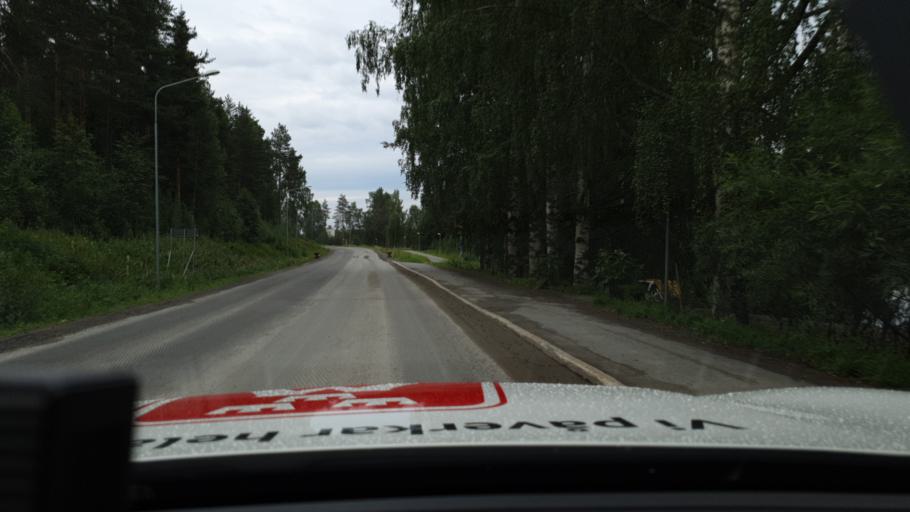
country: SE
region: Norrbotten
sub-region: Bodens Kommun
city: Boden
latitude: 65.8356
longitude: 21.6125
